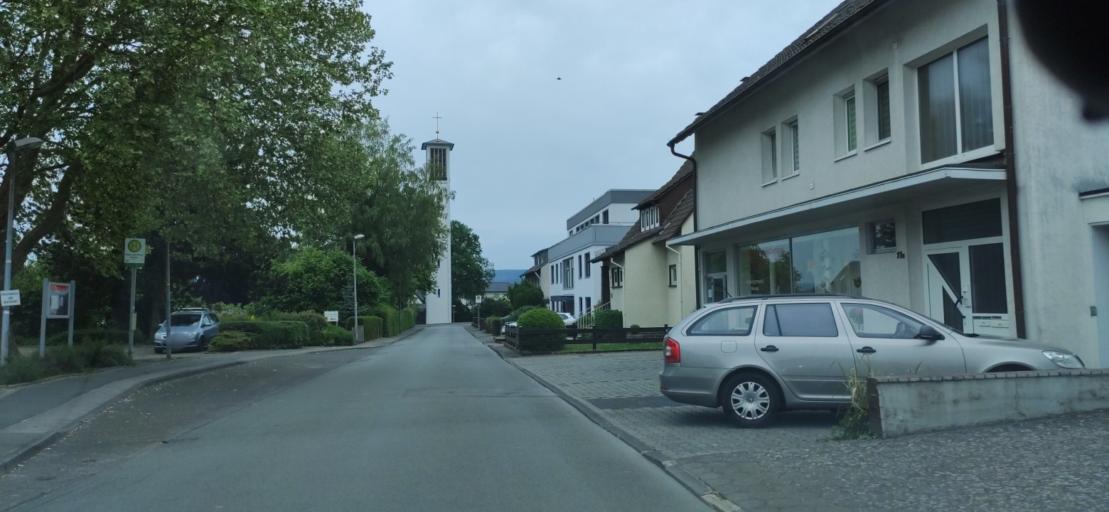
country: DE
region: North Rhine-Westphalia
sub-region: Regierungsbezirk Detmold
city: Hoexter
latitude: 51.7709
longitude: 9.3659
